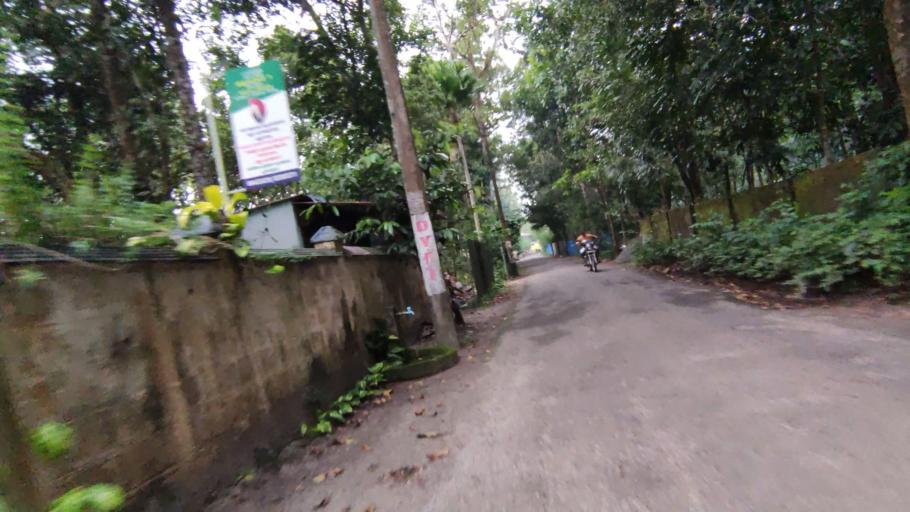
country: IN
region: Kerala
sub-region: Alappuzha
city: Shertallai
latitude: 9.6524
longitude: 76.3682
